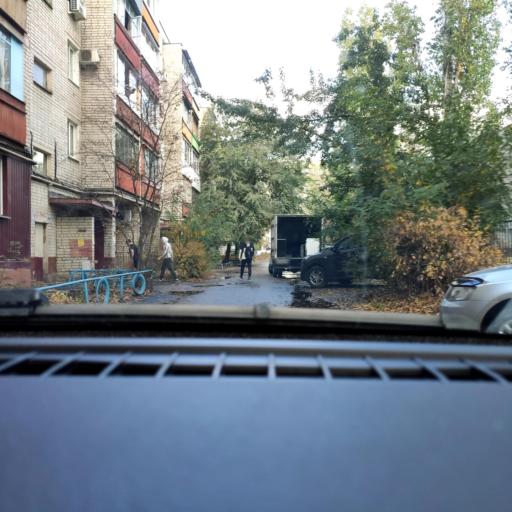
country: RU
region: Voronezj
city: Maslovka
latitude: 51.6390
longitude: 39.2715
